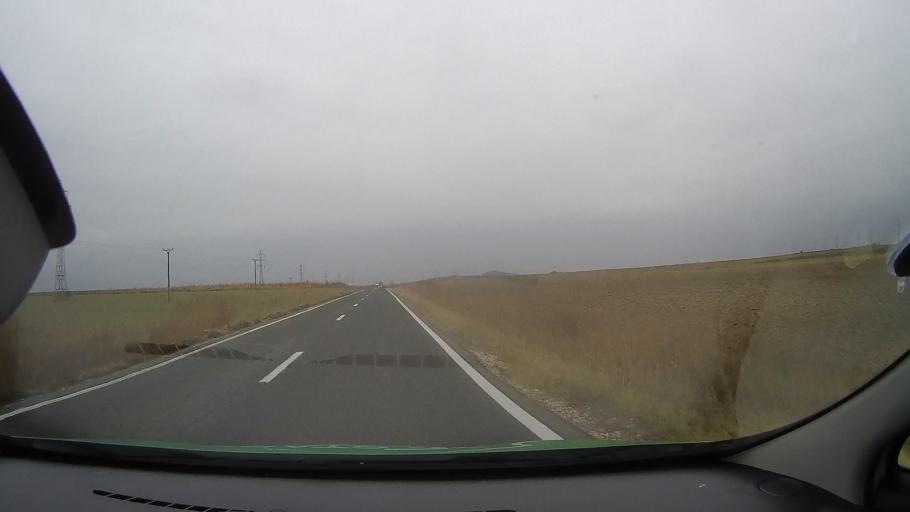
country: RO
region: Constanta
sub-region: Comuna Ciobanu
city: Ciobanu
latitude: 44.6963
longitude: 27.9902
